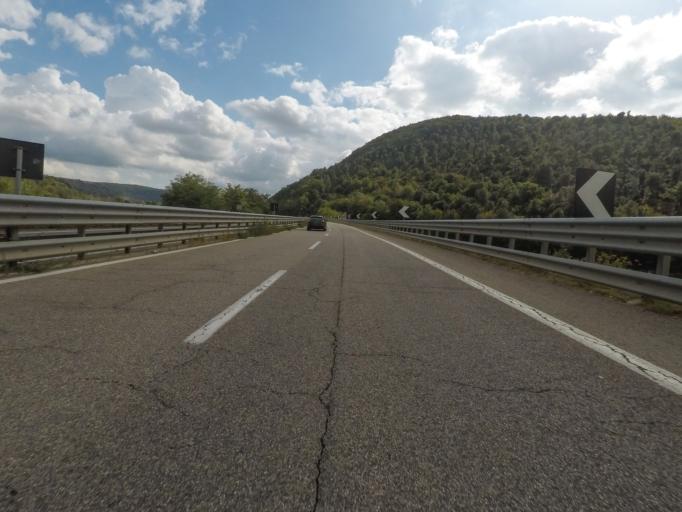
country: IT
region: Tuscany
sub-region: Provincia di Siena
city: Rapolano Terme
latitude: 43.2902
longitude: 11.6135
